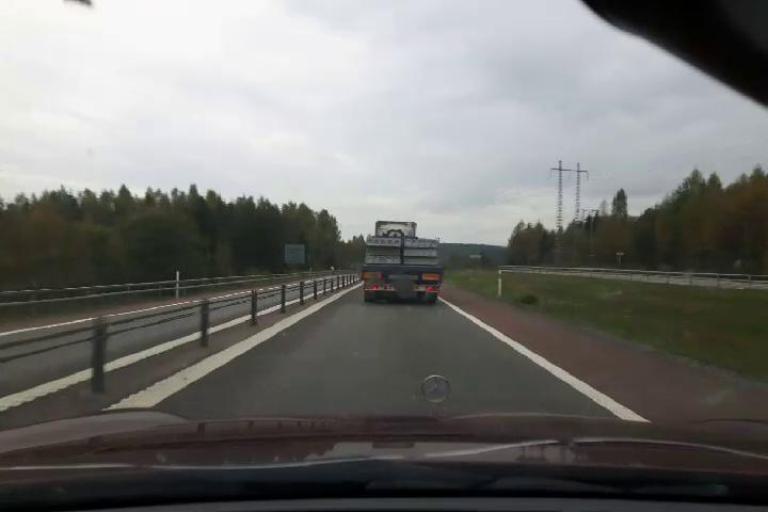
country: SE
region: Vaesternorrland
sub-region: Haernoesands Kommun
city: Haernoesand
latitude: 62.7759
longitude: 17.9190
